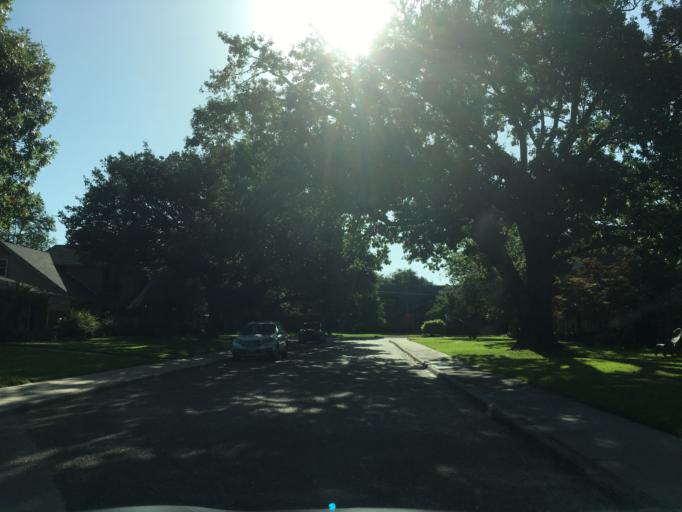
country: US
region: Texas
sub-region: Dallas County
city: Richardson
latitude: 32.8829
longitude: -96.7267
